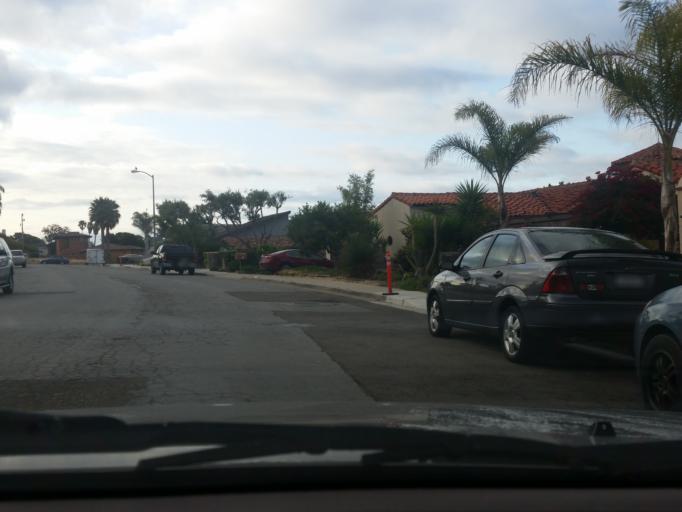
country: US
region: California
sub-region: San Luis Obispo County
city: Pismo Beach
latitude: 35.1585
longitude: -120.6799
